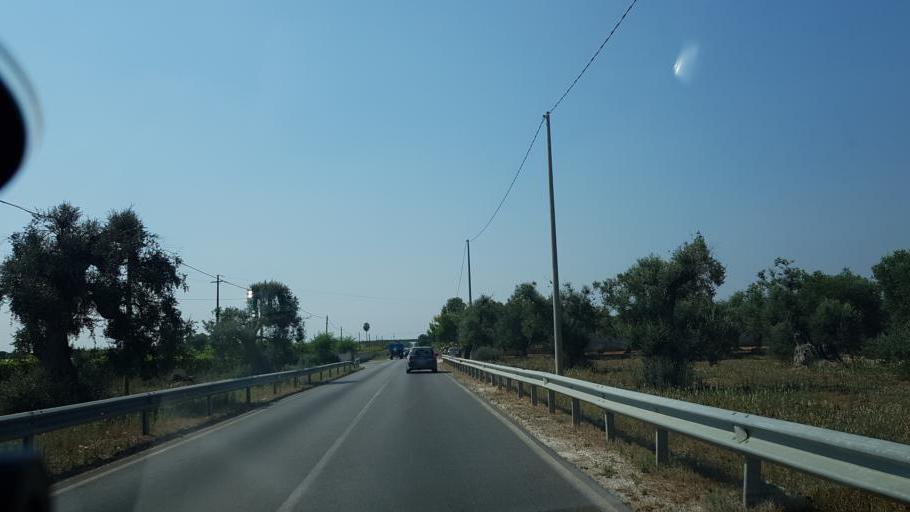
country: IT
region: Apulia
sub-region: Provincia di Taranto
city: Manduria
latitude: 40.4266
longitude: 17.6336
